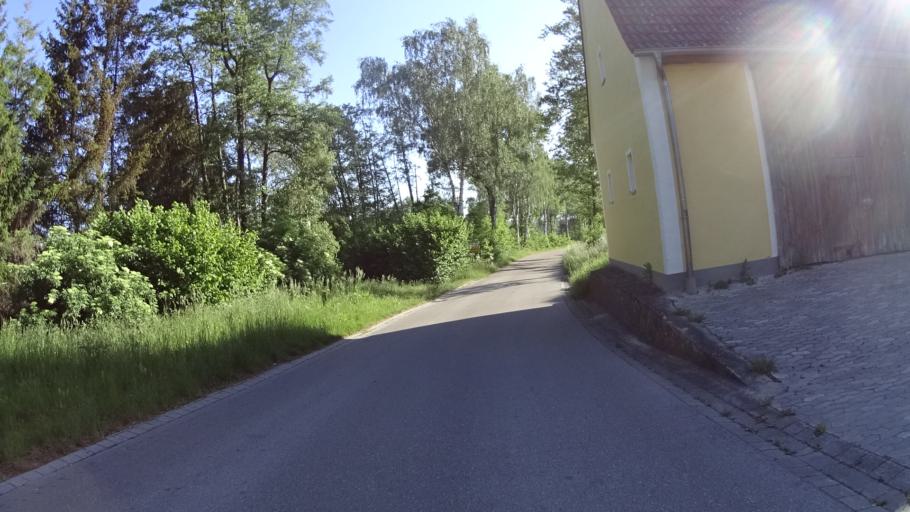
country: DE
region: Bavaria
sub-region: Regierungsbezirk Mittelfranken
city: Wieseth
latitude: 49.1570
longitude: 10.4665
